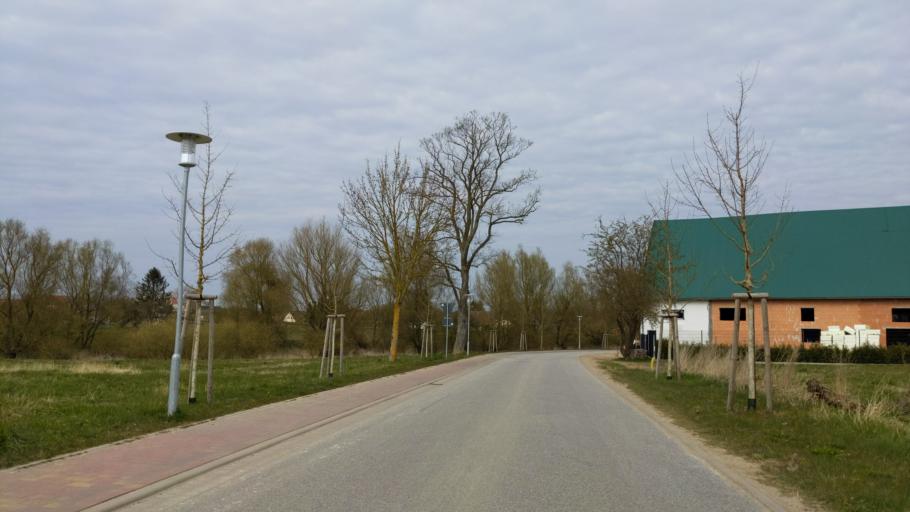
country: DE
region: Mecklenburg-Vorpommern
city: Dassow
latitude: 53.9558
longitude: 10.9728
